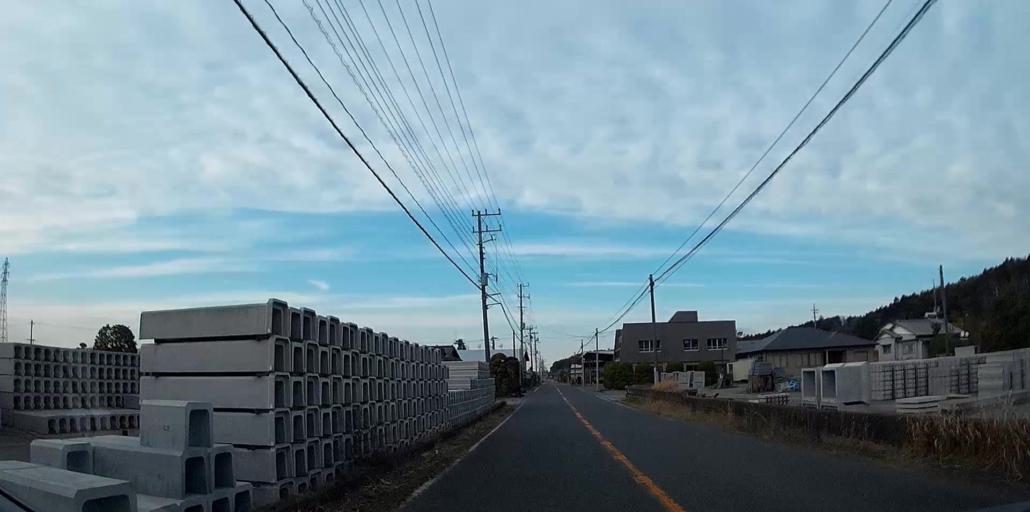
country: JP
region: Chiba
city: Kisarazu
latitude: 35.3460
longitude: 140.0568
